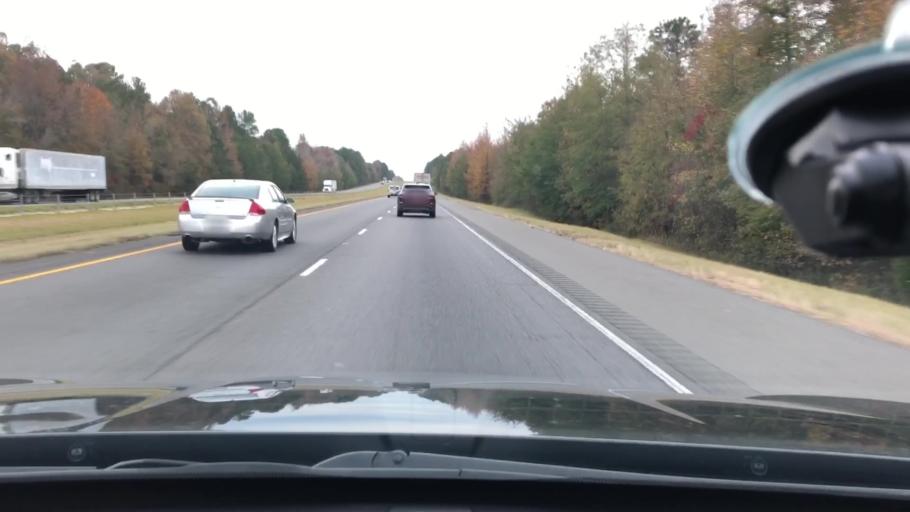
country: US
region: Arkansas
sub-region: Clark County
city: Arkadelphia
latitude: 34.0512
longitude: -93.1337
